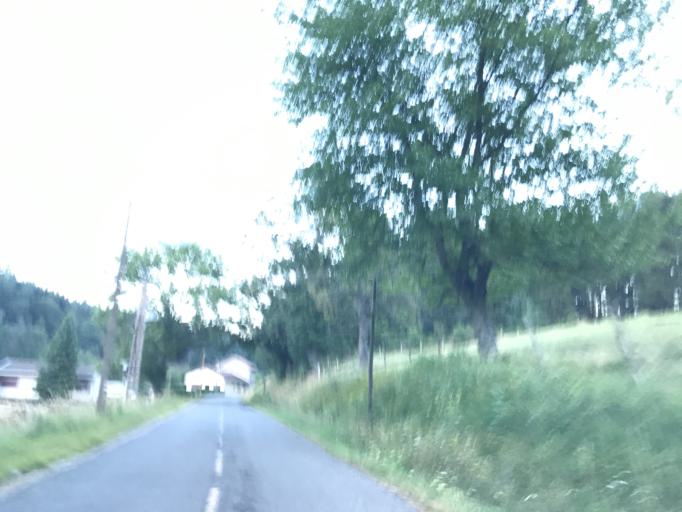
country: FR
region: Rhone-Alpes
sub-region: Departement de la Loire
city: Noiretable
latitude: 45.8210
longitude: 3.7095
